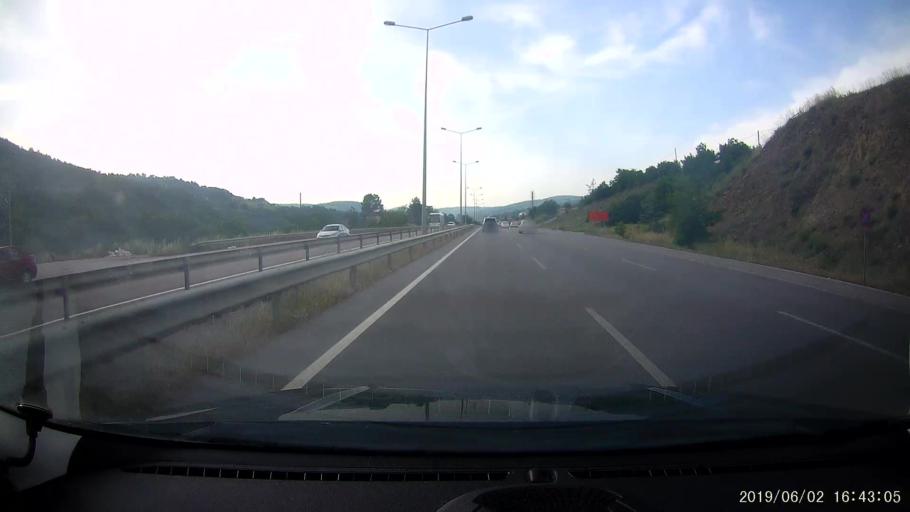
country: TR
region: Samsun
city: Kavak
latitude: 41.1295
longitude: 36.1341
